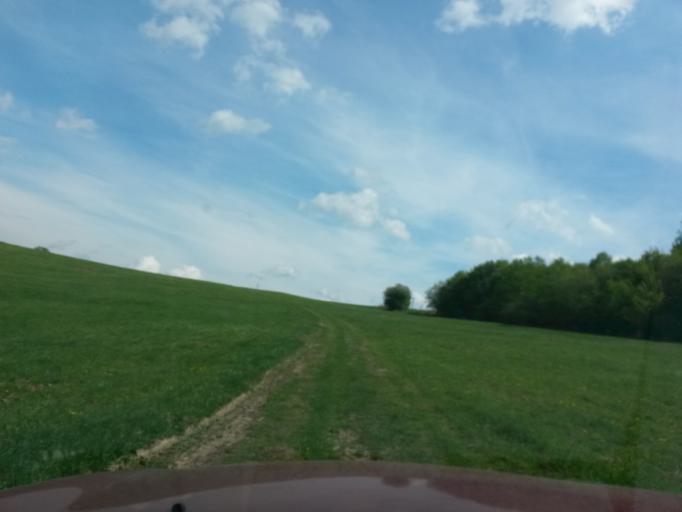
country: SK
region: Kosicky
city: Gelnica
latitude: 48.8308
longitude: 21.0578
